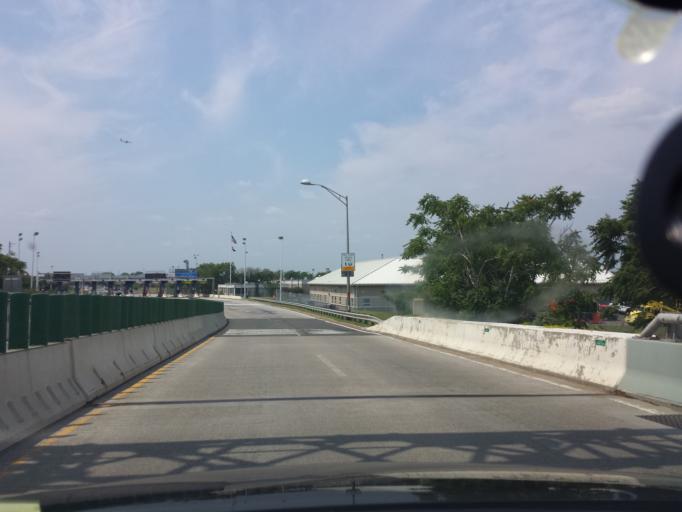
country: US
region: New York
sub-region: Kings County
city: East New York
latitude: 40.5783
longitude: -73.8878
